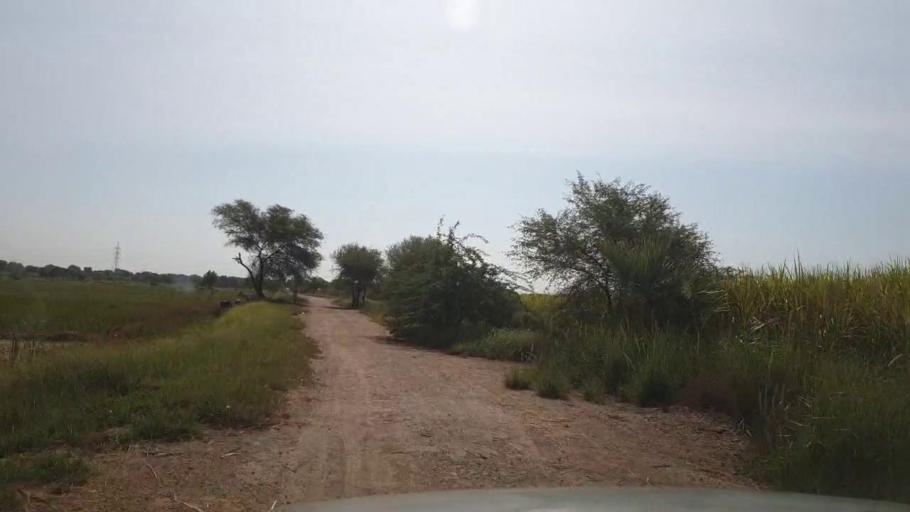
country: PK
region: Sindh
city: Tando Muhammad Khan
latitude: 25.1277
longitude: 68.4225
